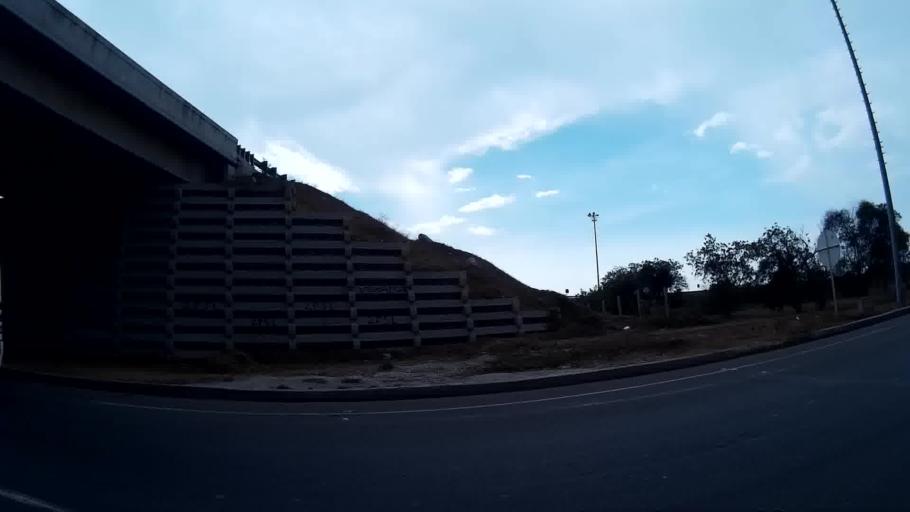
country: CO
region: Magdalena
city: Cienaga
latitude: 11.0052
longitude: -74.2174
